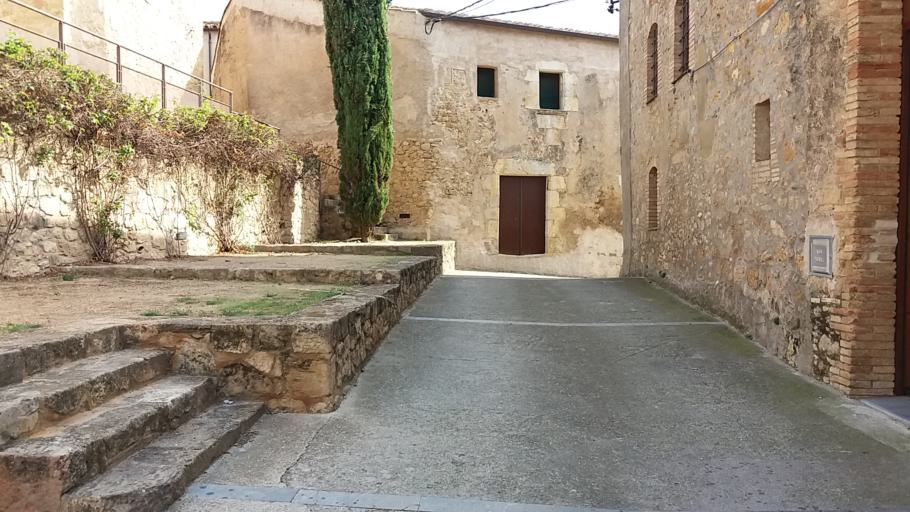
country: ES
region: Catalonia
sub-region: Provincia de Girona
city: Vilademuls
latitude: 42.1242
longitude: 2.9068
